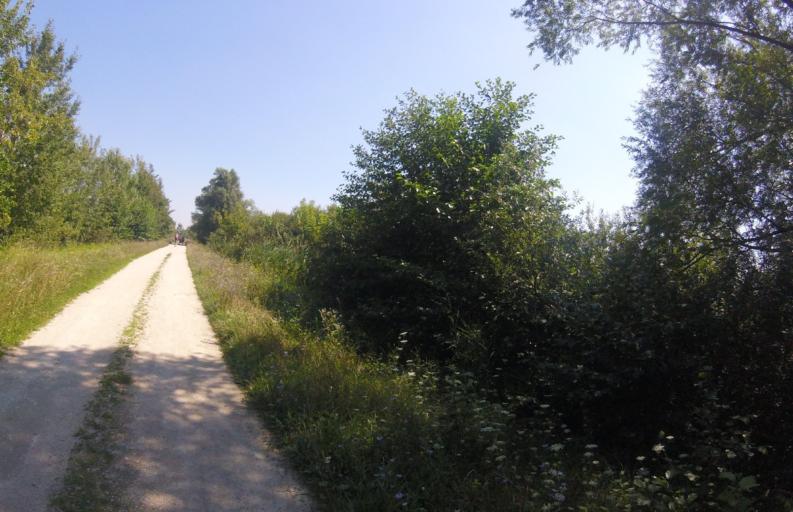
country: HU
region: Zala
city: Sarmellek
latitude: 46.6787
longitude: 17.2321
